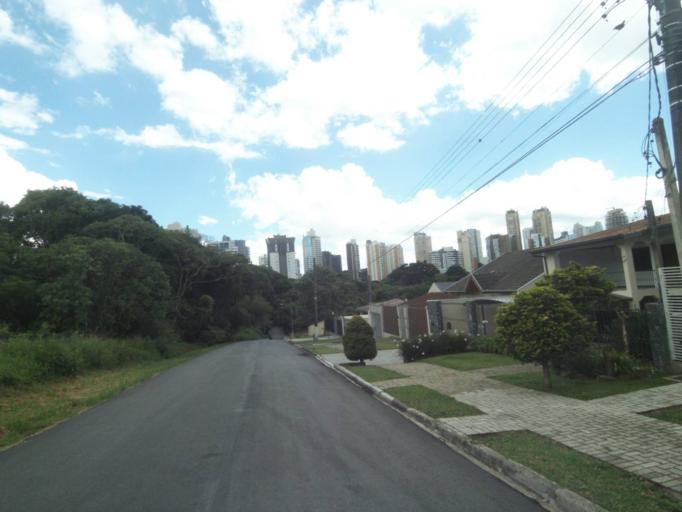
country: BR
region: Parana
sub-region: Curitiba
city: Curitiba
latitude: -25.4331
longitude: -49.3301
